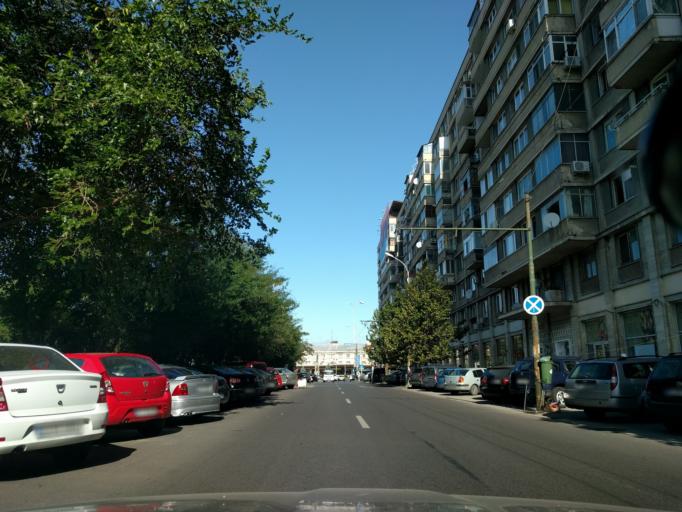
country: RO
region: Bucuresti
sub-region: Municipiul Bucuresti
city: Bucuresti
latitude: 44.4455
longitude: 26.0770
